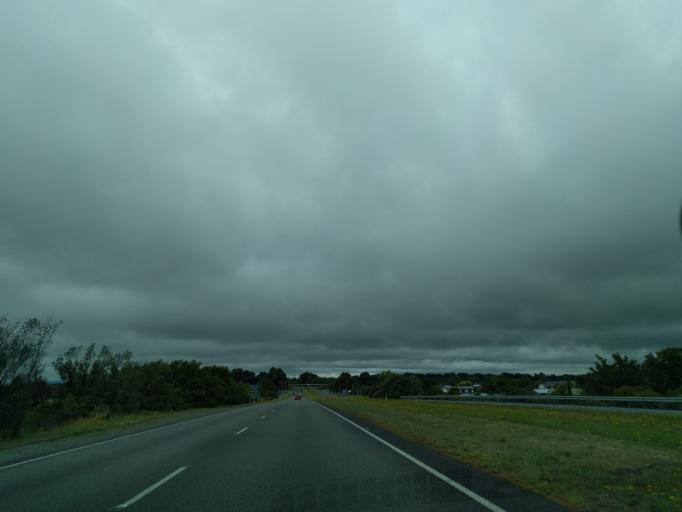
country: NZ
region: Canterbury
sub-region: Waimakariri District
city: Kaiapoi
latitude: -43.3797
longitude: 172.6443
